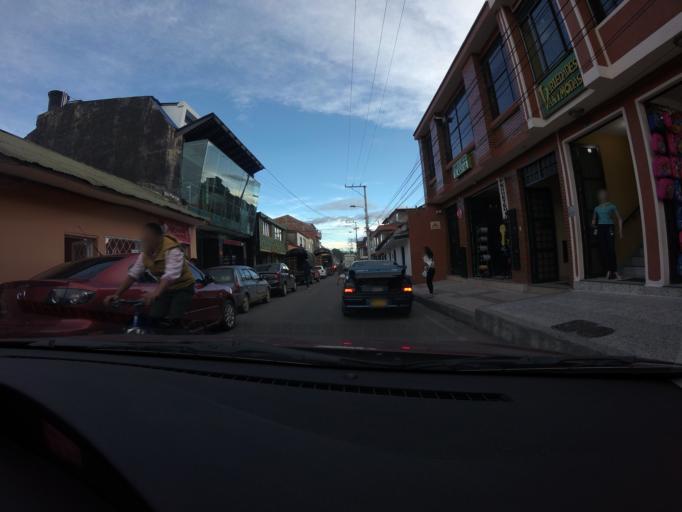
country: CO
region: Cundinamarca
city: Sopo
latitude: 4.9095
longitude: -73.9412
